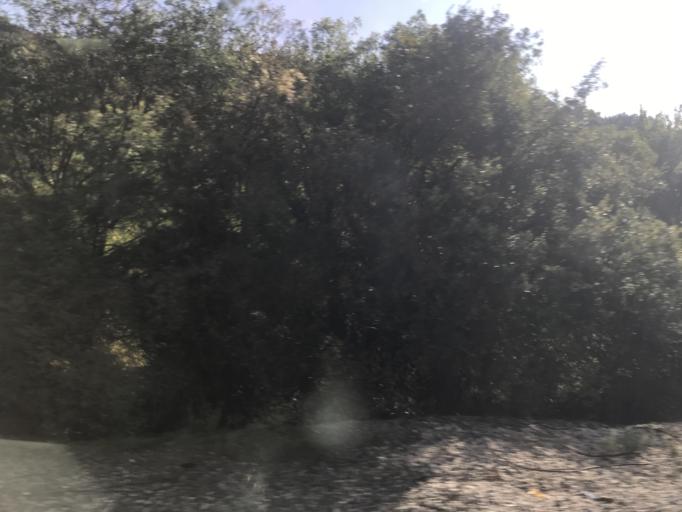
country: ES
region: Basque Country
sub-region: Provincia de Alava
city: Arminon
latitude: 42.7847
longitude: -2.8259
